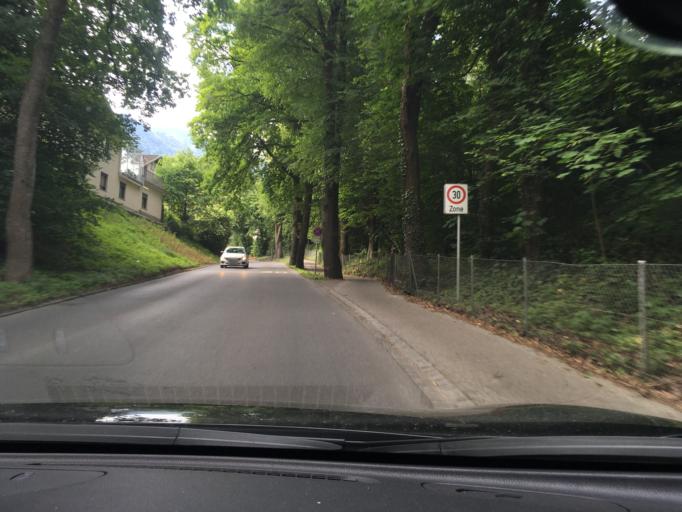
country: AT
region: Vorarlberg
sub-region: Politischer Bezirk Feldkirch
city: Feldkirch
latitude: 47.2321
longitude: 9.5776
